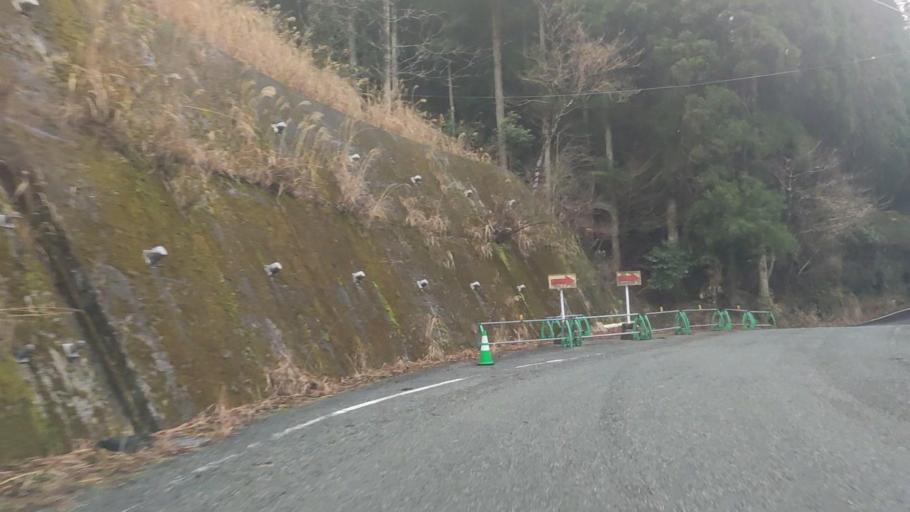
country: JP
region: Kumamoto
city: Matsubase
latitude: 32.5996
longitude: 130.8905
